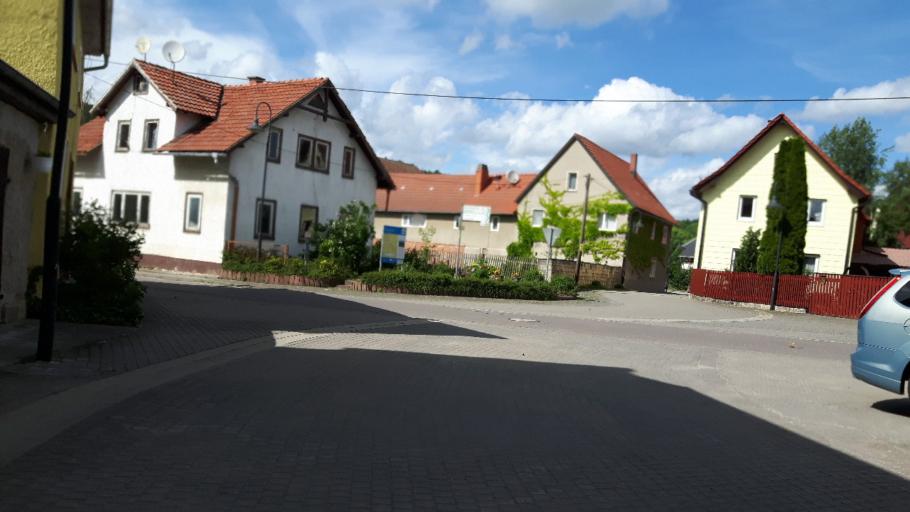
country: DE
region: Thuringia
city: Witzleben
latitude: 50.7889
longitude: 11.1427
